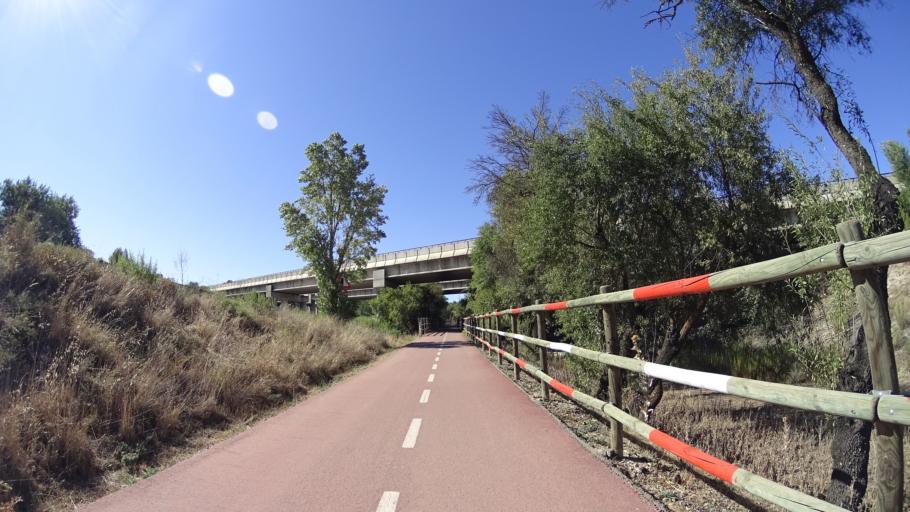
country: ES
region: Madrid
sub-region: Provincia de Madrid
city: Arganda
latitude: 40.2741
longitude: -3.4497
